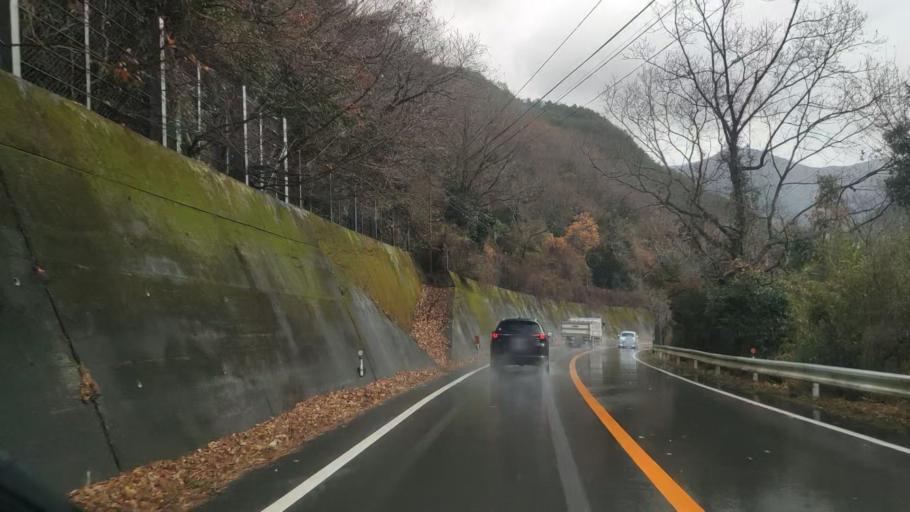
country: JP
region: Tokushima
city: Kamojimacho-jogejima
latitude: 34.1657
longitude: 134.3448
